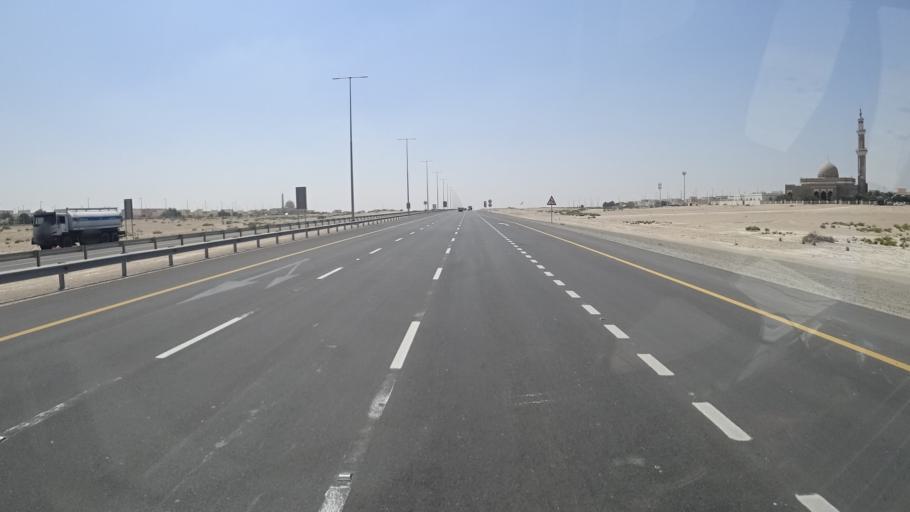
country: AE
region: Abu Dhabi
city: Abu Dhabi
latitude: 24.3325
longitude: 54.6948
